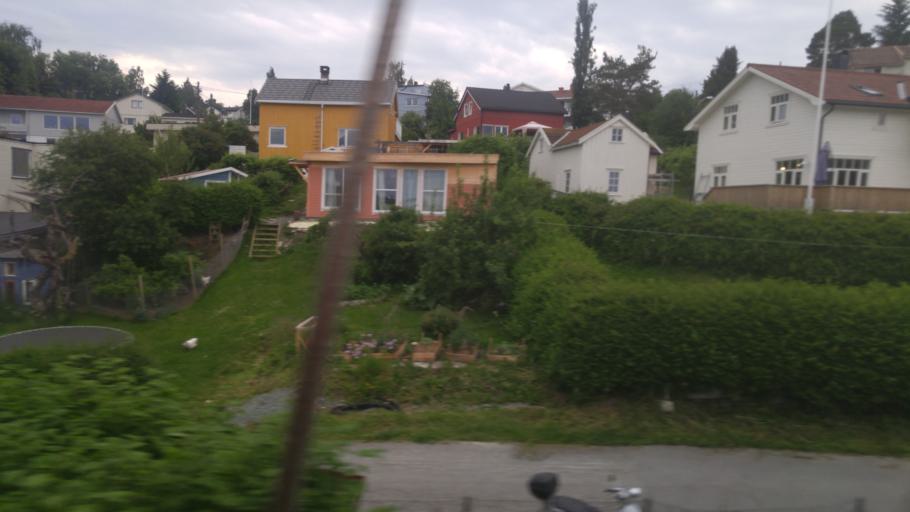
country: NO
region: Sor-Trondelag
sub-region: Malvik
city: Malvik
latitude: 63.4405
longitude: 10.6080
